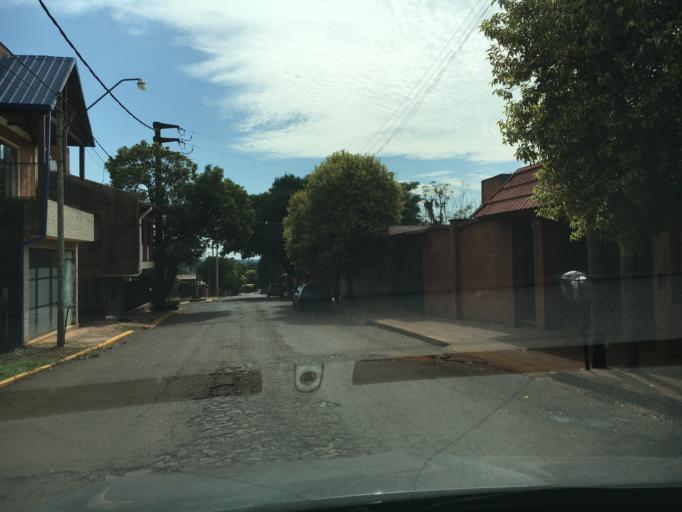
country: AR
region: Misiones
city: Puerto Rico
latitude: -26.8160
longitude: -55.0281
